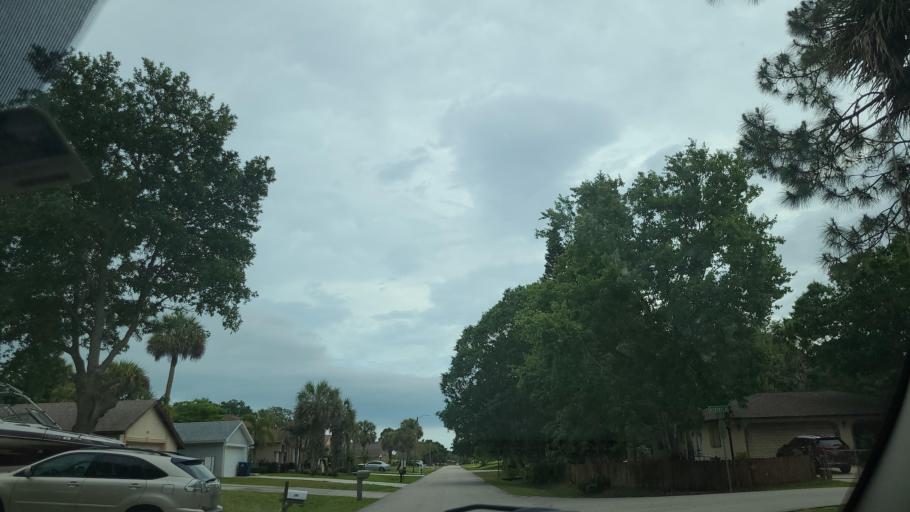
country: US
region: Florida
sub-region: Brevard County
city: West Melbourne
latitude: 28.0126
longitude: -80.6631
